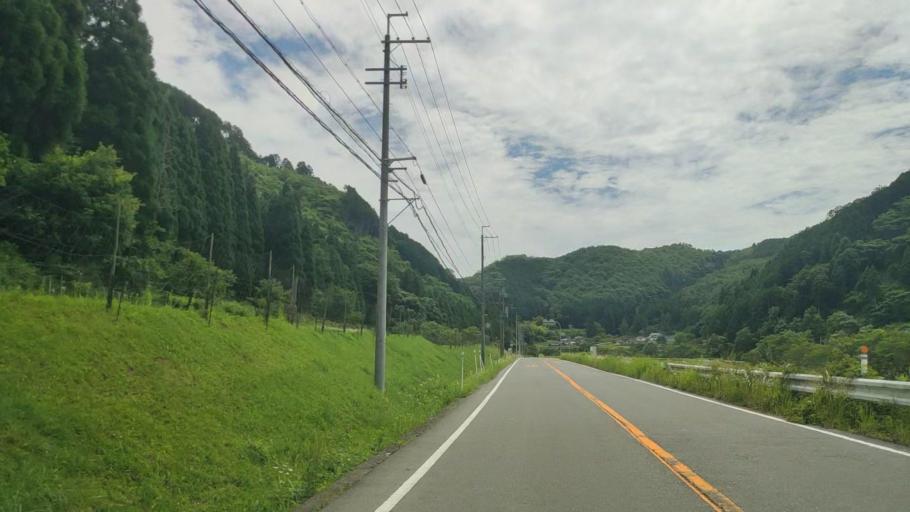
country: JP
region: Hyogo
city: Yamazakicho-nakabirose
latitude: 35.0872
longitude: 134.3594
